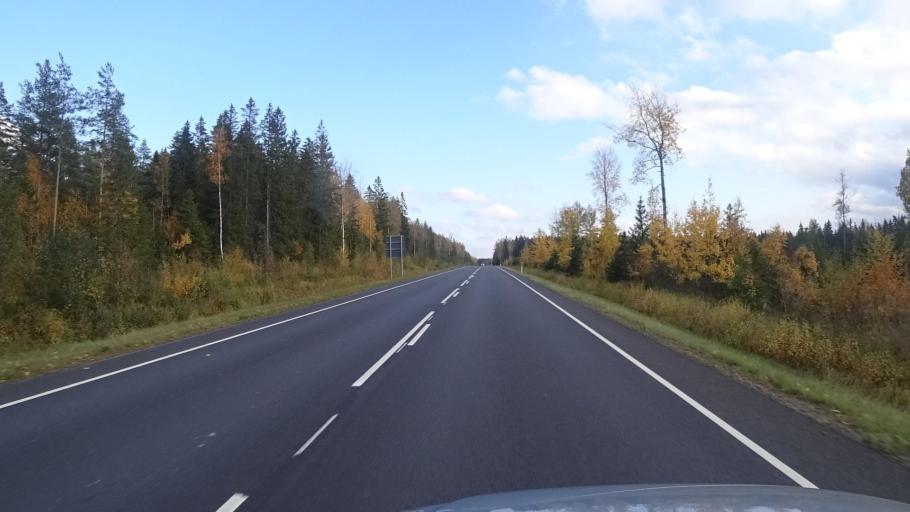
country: FI
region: Satakunta
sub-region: Rauma
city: Eura
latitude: 61.1151
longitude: 22.1956
